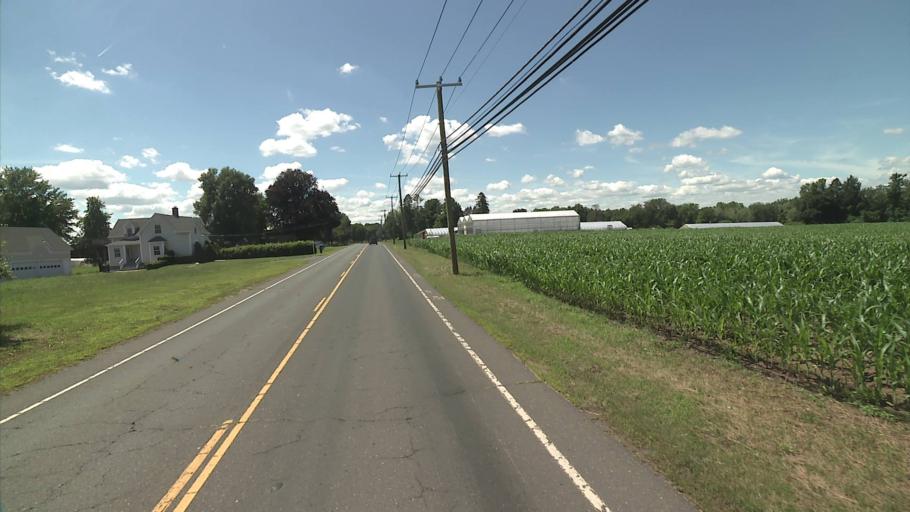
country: US
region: Connecticut
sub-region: Hartford County
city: Suffield Depot
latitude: 41.9833
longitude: -72.6709
